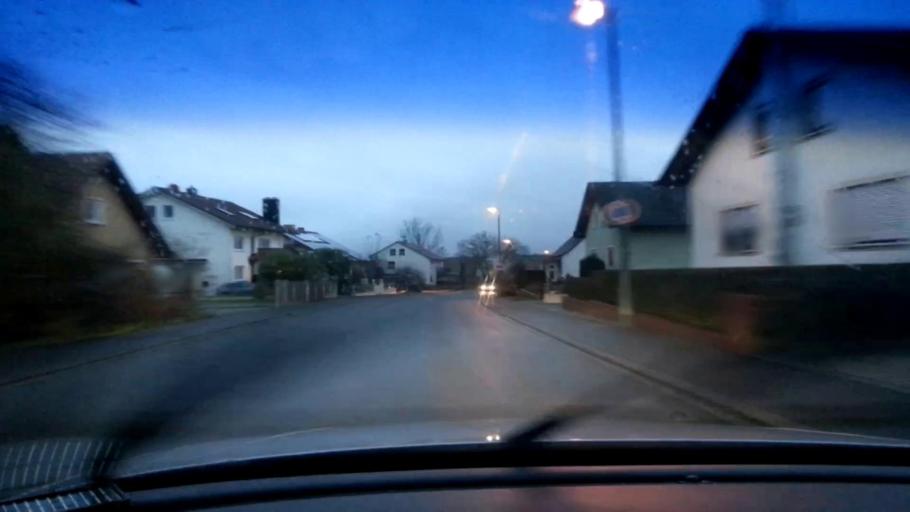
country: DE
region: Bavaria
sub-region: Upper Franconia
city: Memmelsdorf
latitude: 49.9558
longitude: 10.9567
